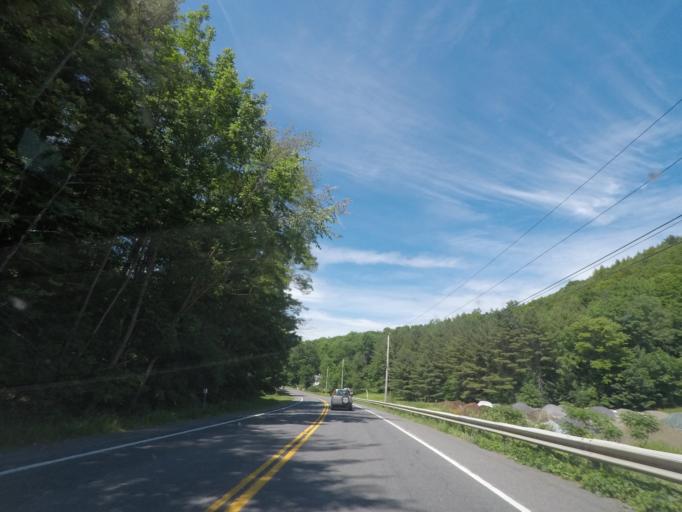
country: US
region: Massachusetts
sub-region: Berkshire County
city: Richmond
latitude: 42.3973
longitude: -73.4091
